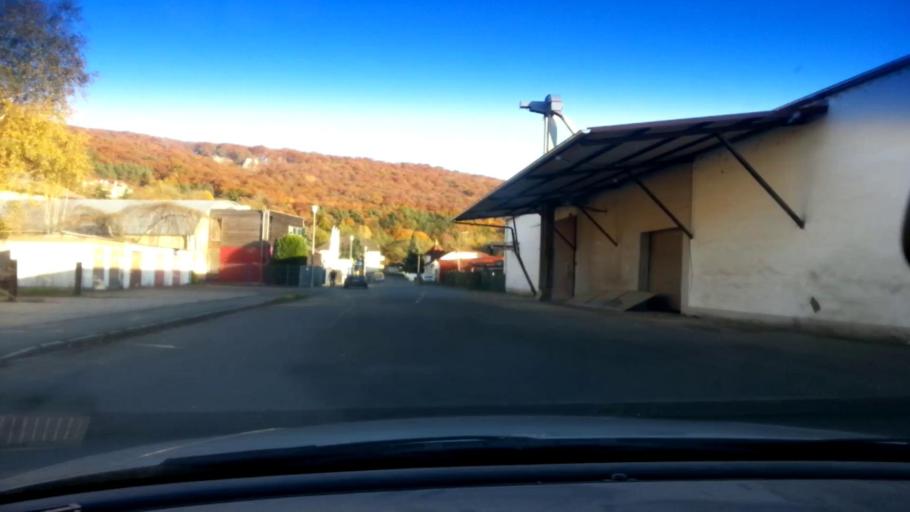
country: DE
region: Bavaria
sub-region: Upper Franconia
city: Heiligenstadt
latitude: 49.8626
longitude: 11.1730
